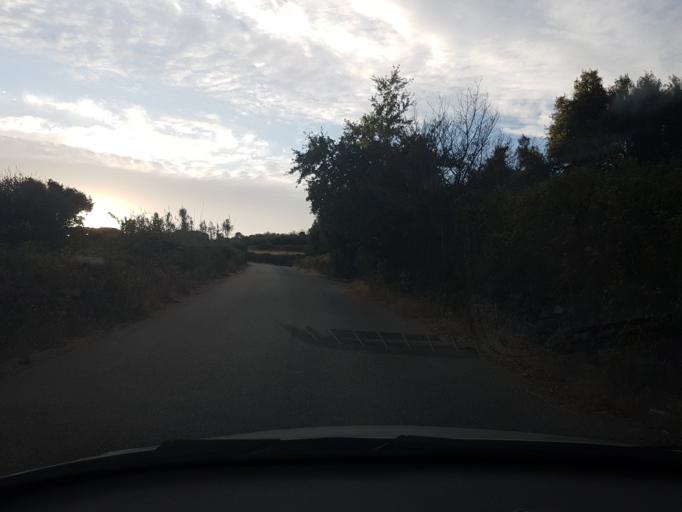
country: IT
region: Sardinia
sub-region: Provincia di Oristano
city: Seneghe
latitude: 40.0979
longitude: 8.6266
